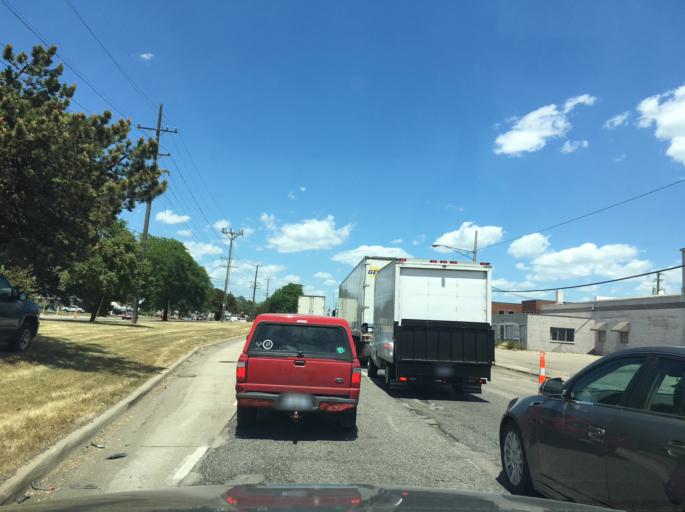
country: US
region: Michigan
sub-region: Macomb County
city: Warren
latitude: 42.4742
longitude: -83.0452
